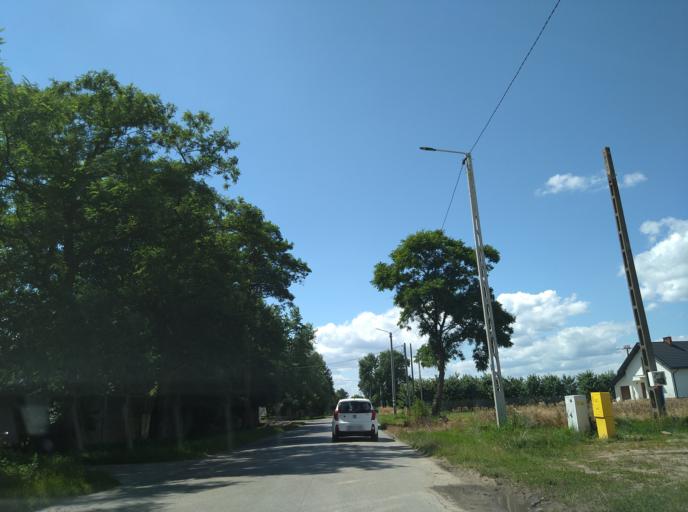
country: PL
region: Masovian Voivodeship
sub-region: Powiat bialobrzeski
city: Bialobrzegi
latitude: 51.6709
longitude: 20.9058
